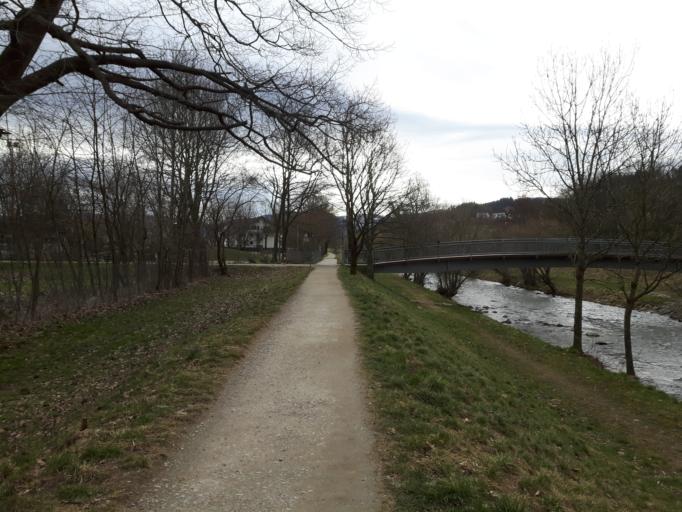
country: DE
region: Baden-Wuerttemberg
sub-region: Freiburg Region
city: Kirchzarten
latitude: 47.9843
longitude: 7.9024
